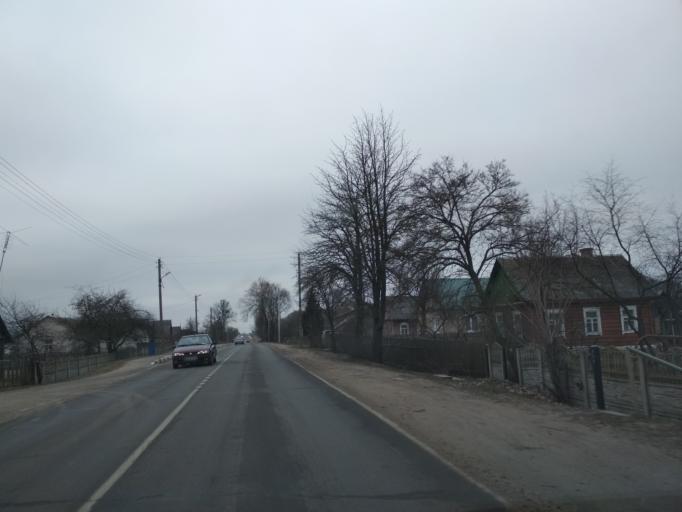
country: BY
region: Minsk
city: Mar''ina Horka
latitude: 53.4990
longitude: 28.1477
